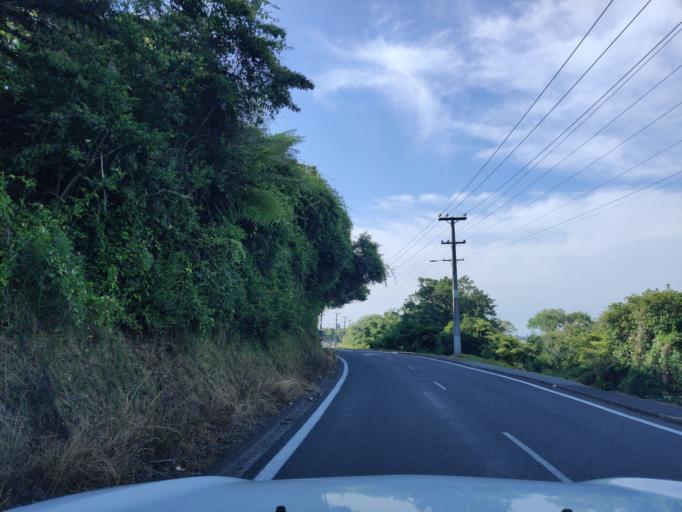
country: NZ
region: Waikato
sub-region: Waikato District
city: Ngaruawahia
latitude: -37.5761
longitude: 175.1532
